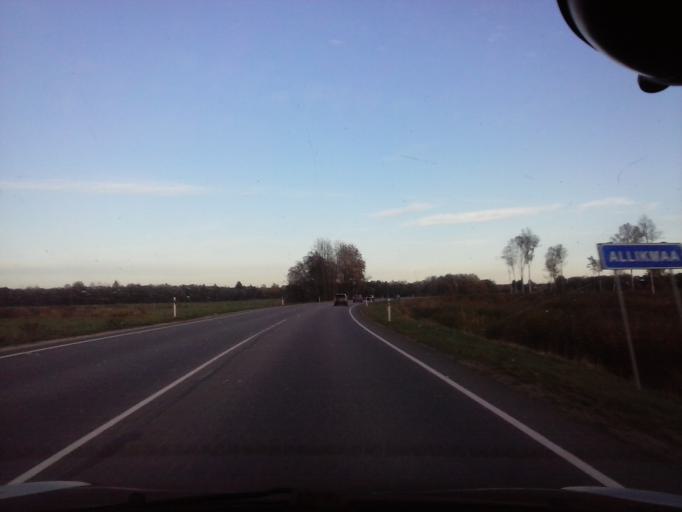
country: EE
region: Laeaene
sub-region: Ridala Parish
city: Uuemoisa
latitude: 58.9730
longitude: 23.8482
